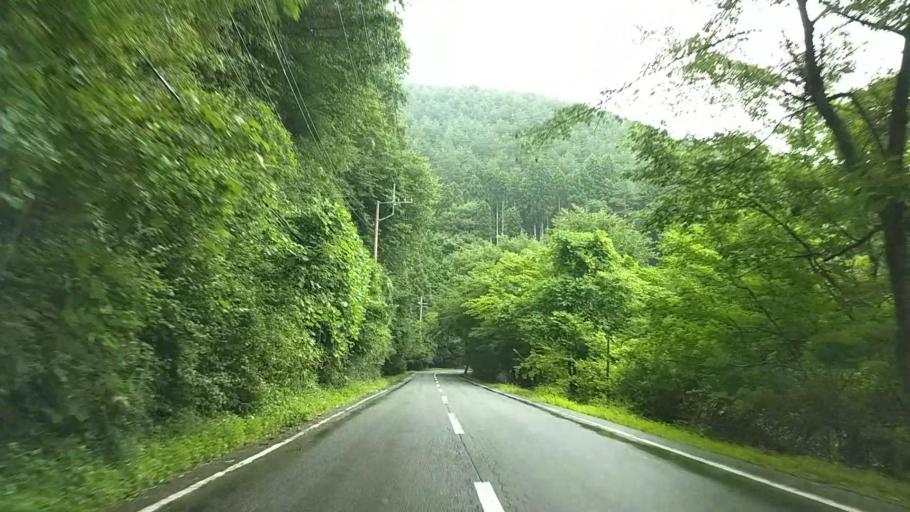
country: JP
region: Yamanashi
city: Fujikawaguchiko
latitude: 35.4816
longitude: 138.6059
